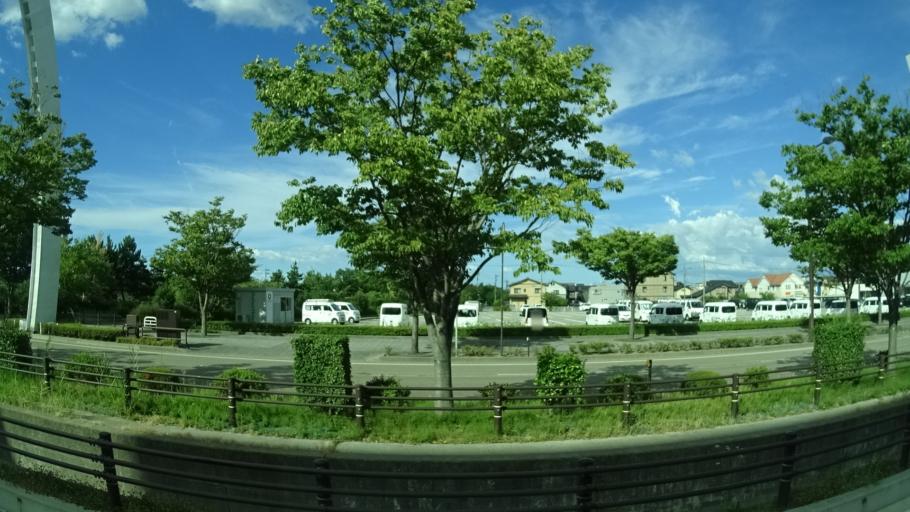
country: JP
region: Ishikawa
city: Kanazawa-shi
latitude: 36.6002
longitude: 136.6218
